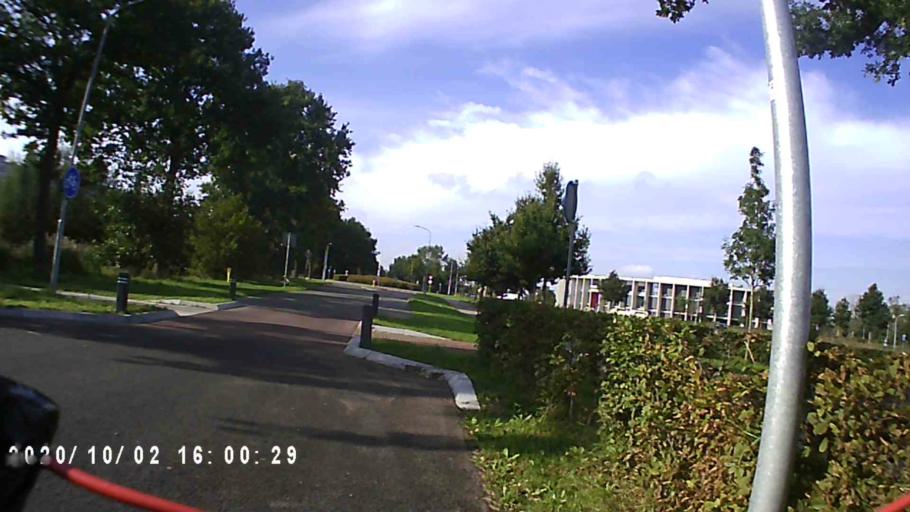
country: NL
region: Groningen
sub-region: Gemeente Zuidhorn
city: Zuidhorn
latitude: 53.2488
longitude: 6.4084
